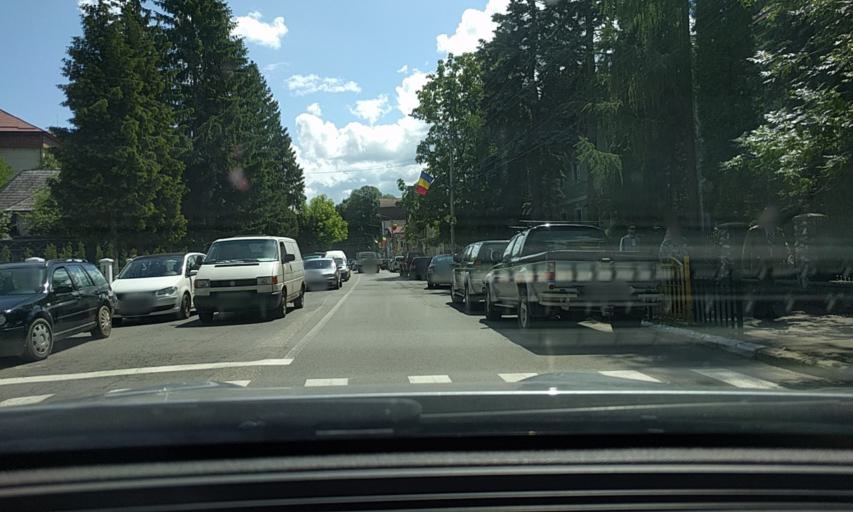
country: RO
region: Bistrita-Nasaud
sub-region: Oras Nasaud
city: Nasaud
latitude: 47.2838
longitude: 24.4072
